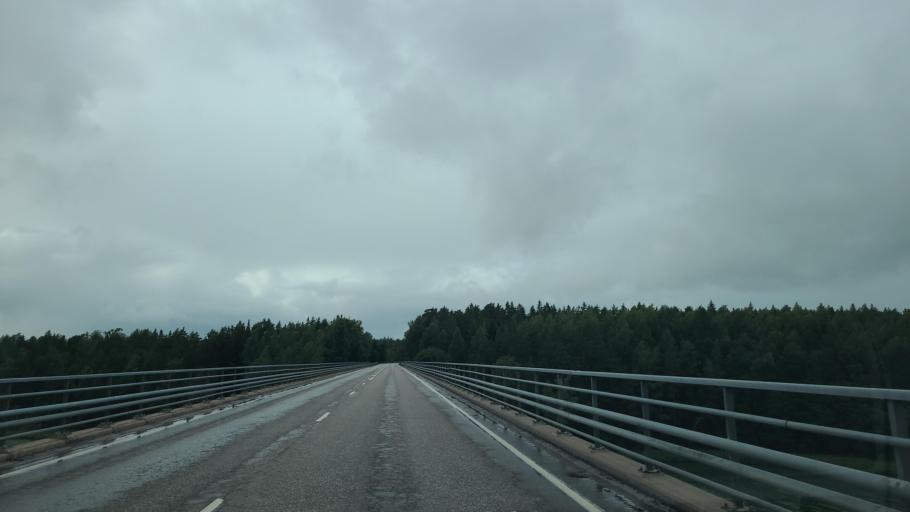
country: FI
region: Varsinais-Suomi
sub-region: Aboland-Turunmaa
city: Kimito
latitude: 60.2295
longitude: 22.6106
